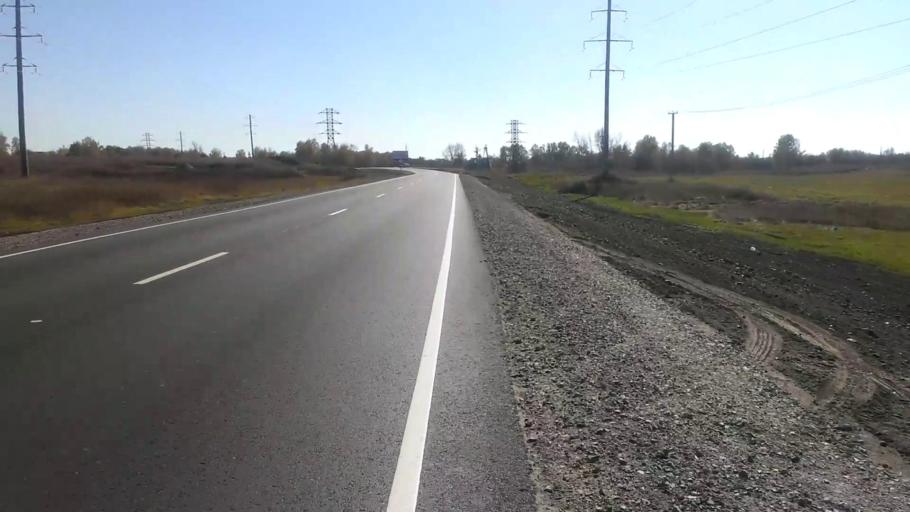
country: RU
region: Altai Krai
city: Sannikovo
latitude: 53.3316
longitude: 83.9382
